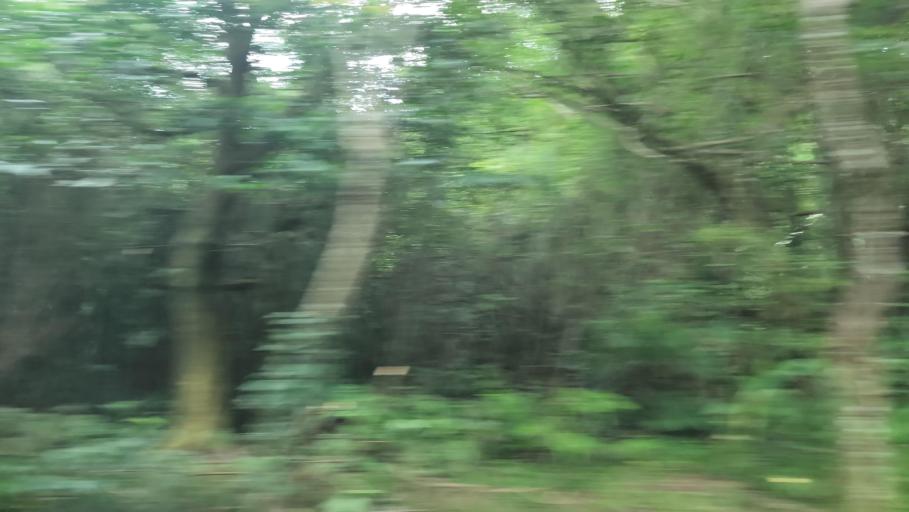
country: TW
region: Taiwan
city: Daxi
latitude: 24.8848
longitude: 121.4178
